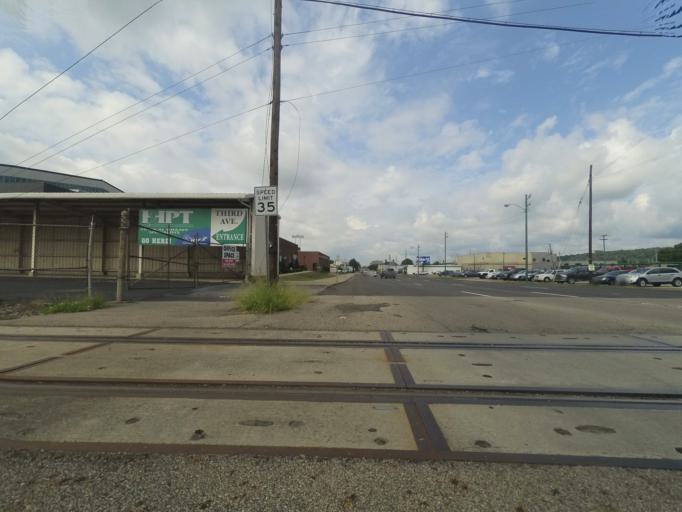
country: US
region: West Virginia
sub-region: Cabell County
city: Huntington
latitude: 38.4263
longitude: -82.4186
